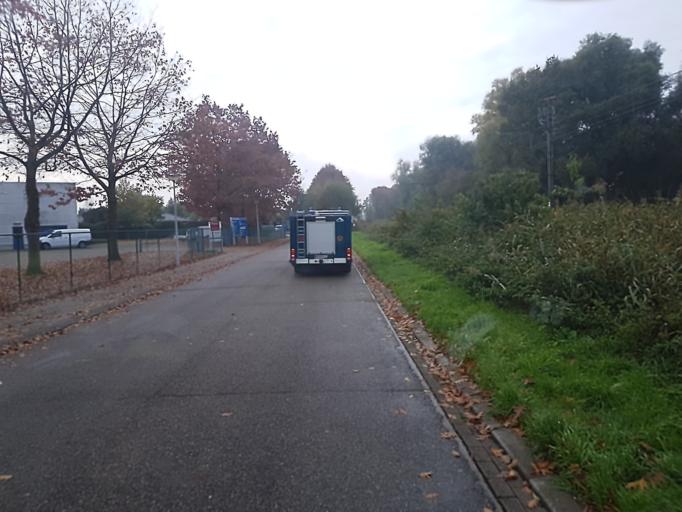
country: BE
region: Flanders
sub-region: Provincie Antwerpen
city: Turnhout
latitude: 51.3114
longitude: 4.9323
